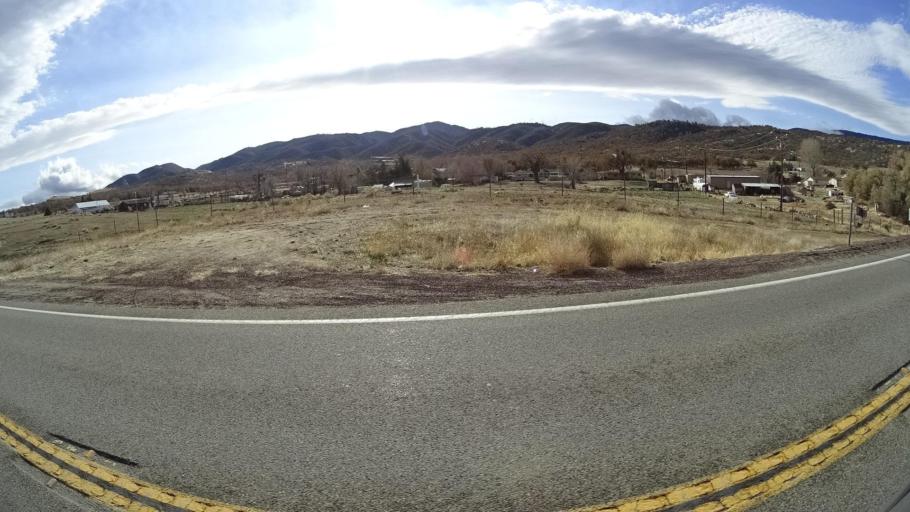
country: US
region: California
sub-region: Kern County
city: Golden Hills
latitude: 35.1118
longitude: -118.5123
